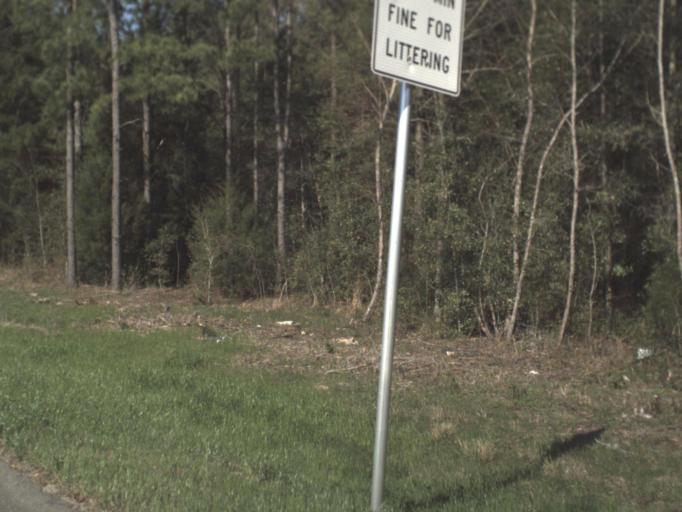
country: US
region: Florida
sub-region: Jackson County
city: Marianna
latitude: 30.7007
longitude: -85.1841
